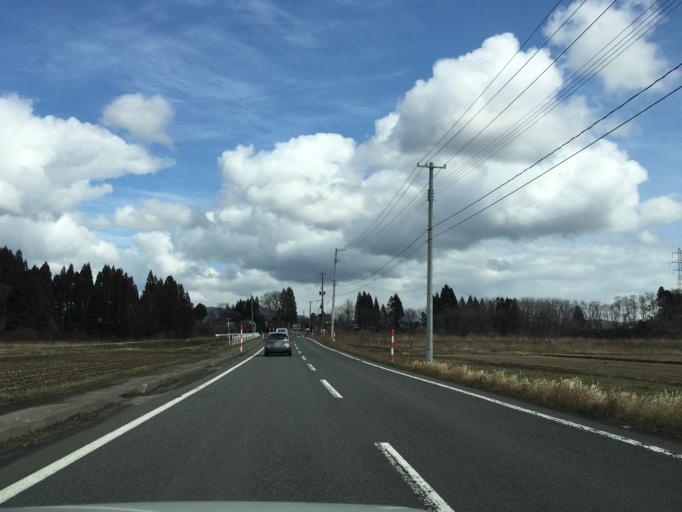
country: JP
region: Akita
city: Odate
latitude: 40.2057
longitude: 140.5606
